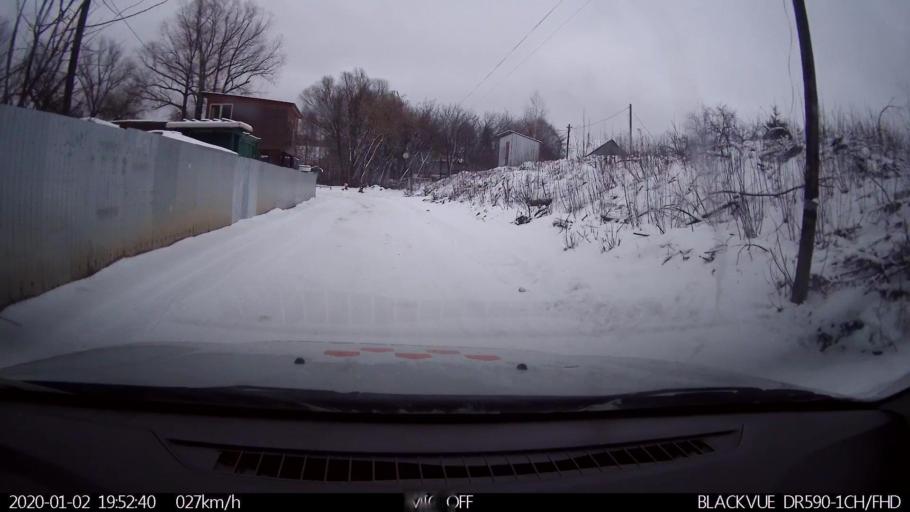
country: RU
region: Nizjnij Novgorod
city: Nizhniy Novgorod
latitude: 56.2725
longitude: 43.9577
